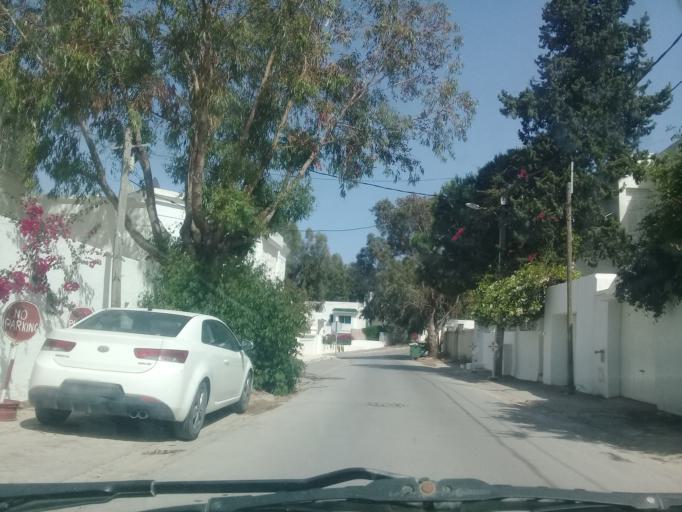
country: TN
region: Tunis
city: Sidi Bou Said
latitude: 36.8810
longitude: 10.3382
